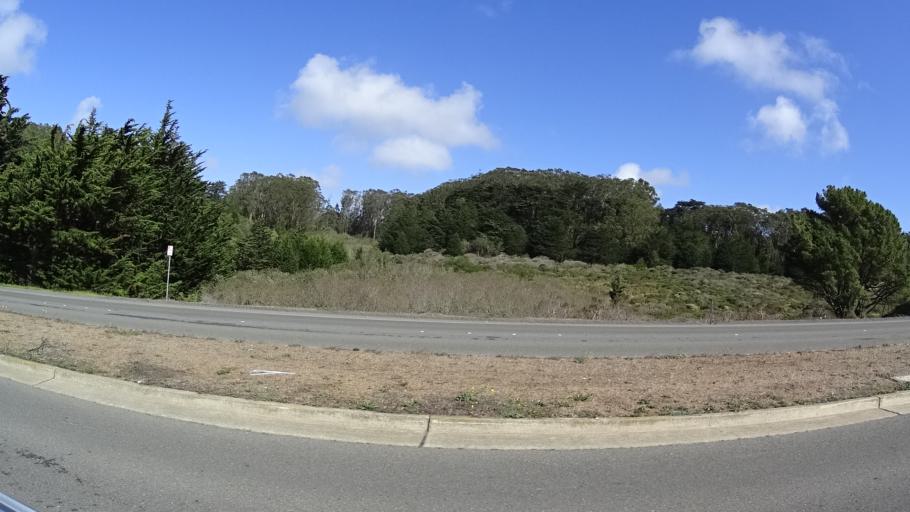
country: US
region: California
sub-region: San Mateo County
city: Daly City
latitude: 37.6975
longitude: -122.4383
